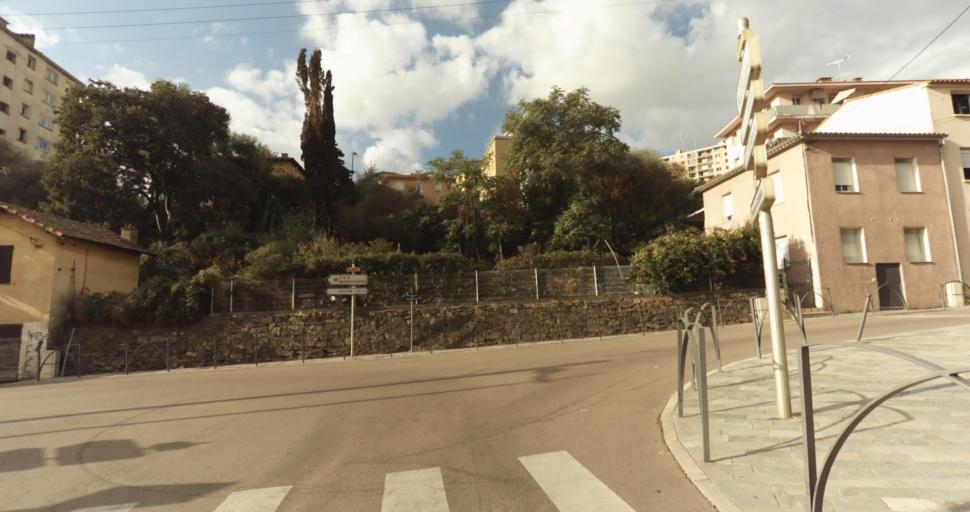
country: FR
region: Corsica
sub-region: Departement de la Corse-du-Sud
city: Ajaccio
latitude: 41.9290
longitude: 8.7329
